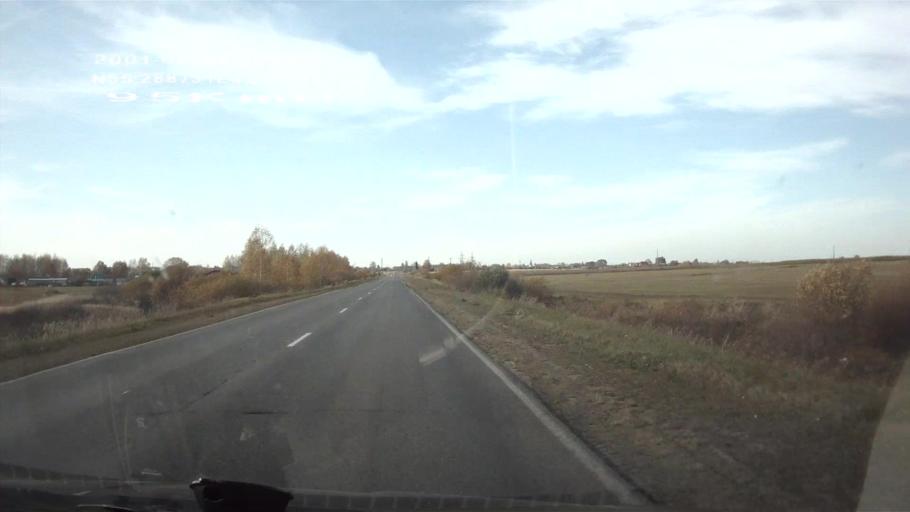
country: RU
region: Chuvashia
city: Ibresi
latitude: 55.2887
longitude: 47.0688
